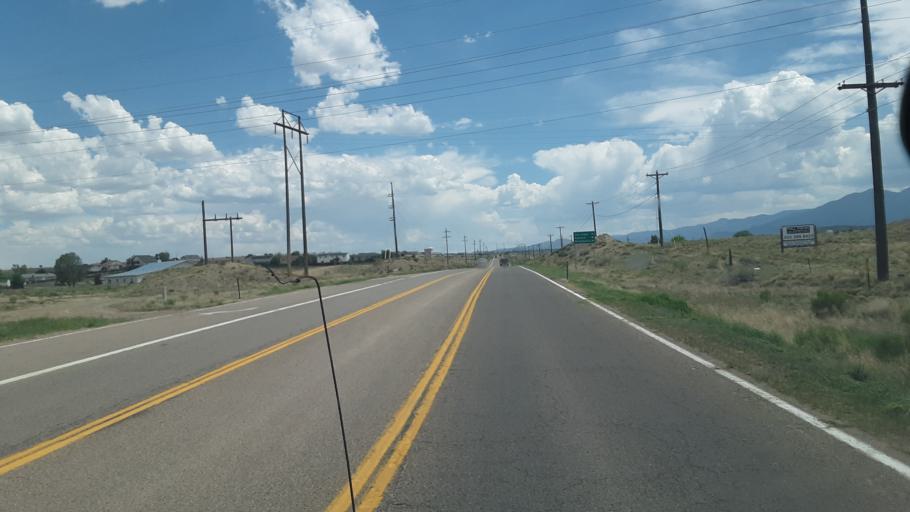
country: US
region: Colorado
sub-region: Fremont County
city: Florence
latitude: 38.3778
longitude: -105.1110
